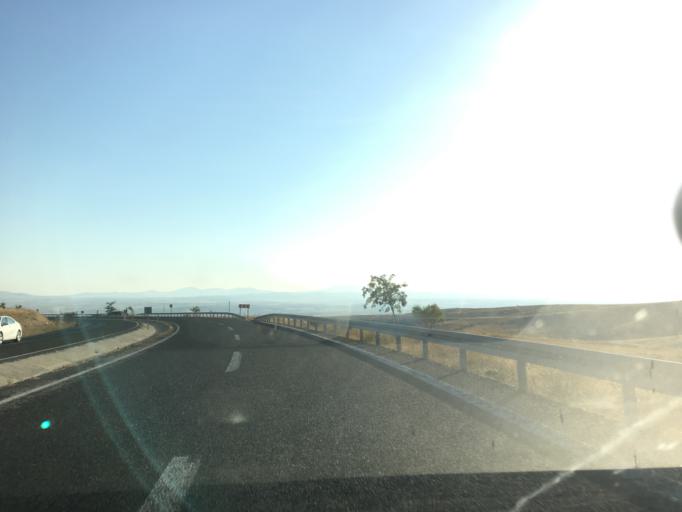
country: TR
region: Nevsehir
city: Salanda
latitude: 38.8507
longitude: 34.5595
